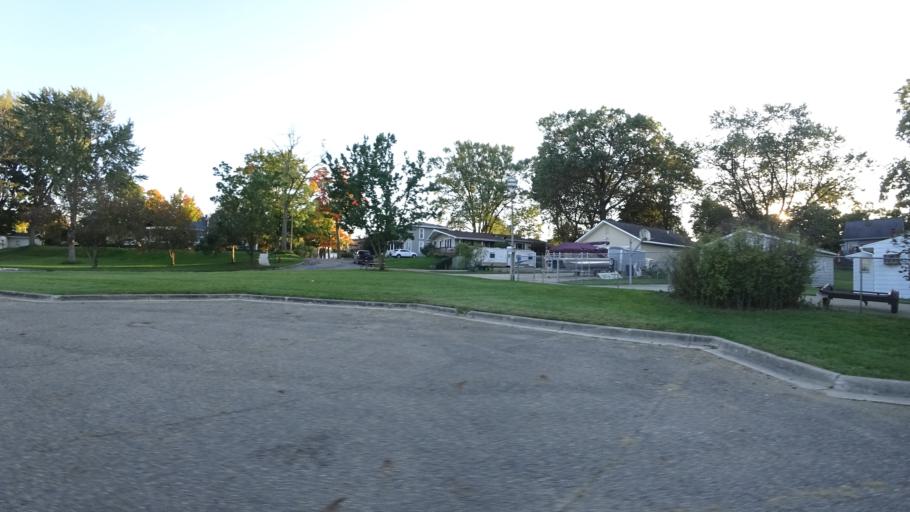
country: US
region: Michigan
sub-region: Saint Joseph County
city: Three Rivers
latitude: 41.9441
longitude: -85.6382
